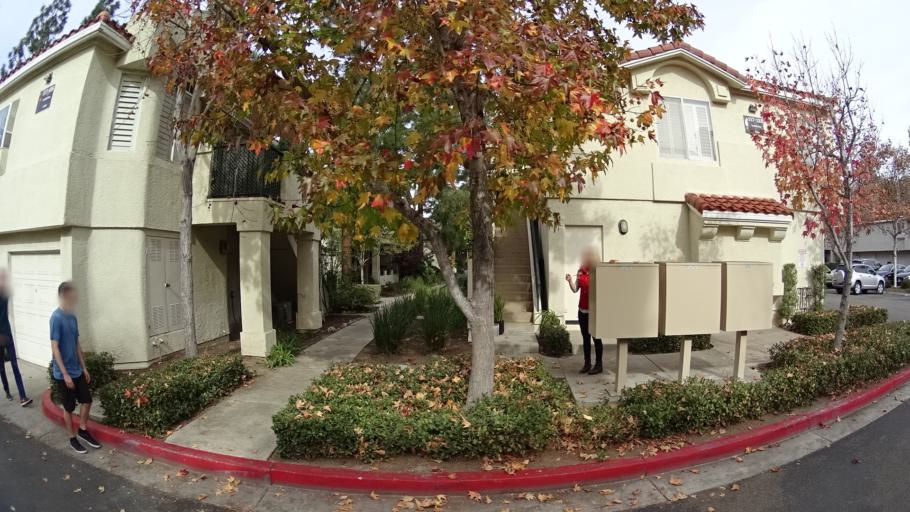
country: US
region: California
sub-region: Orange County
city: Laguna Woods
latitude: 33.5987
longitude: -117.7437
